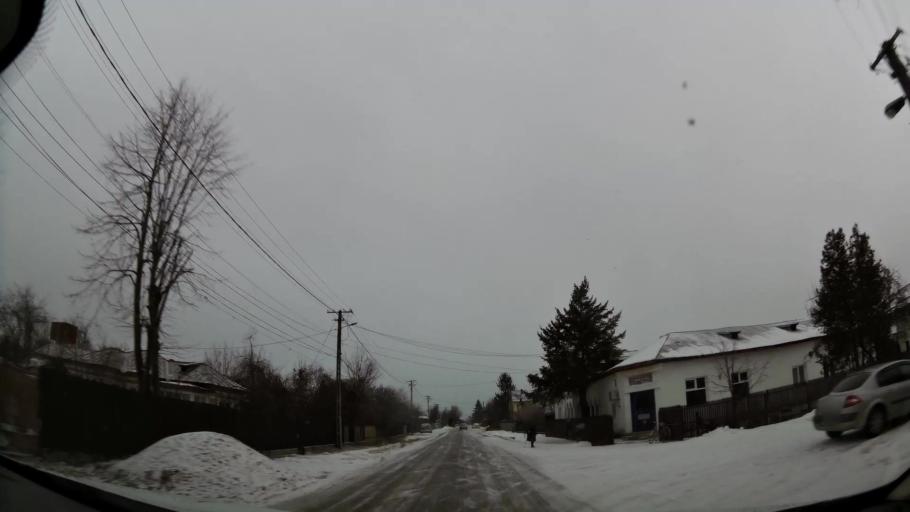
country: RO
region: Prahova
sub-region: Comuna Poenarii-Burchi
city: Ologeni
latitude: 44.7333
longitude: 25.9443
